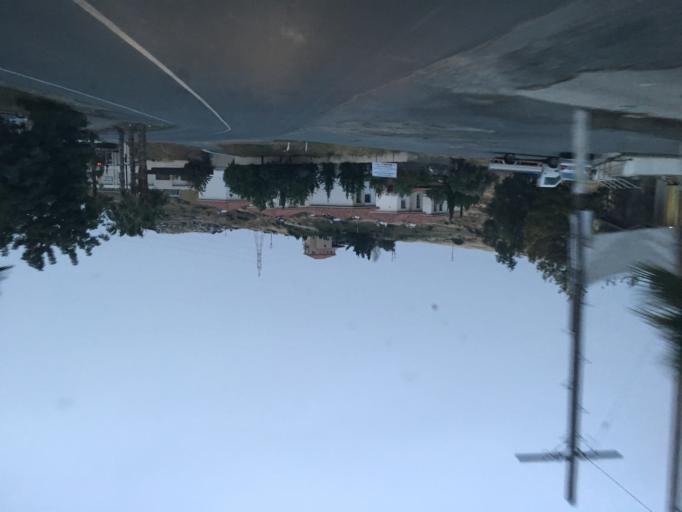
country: CY
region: Limassol
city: Parekklisha
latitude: 34.7377
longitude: 33.1615
